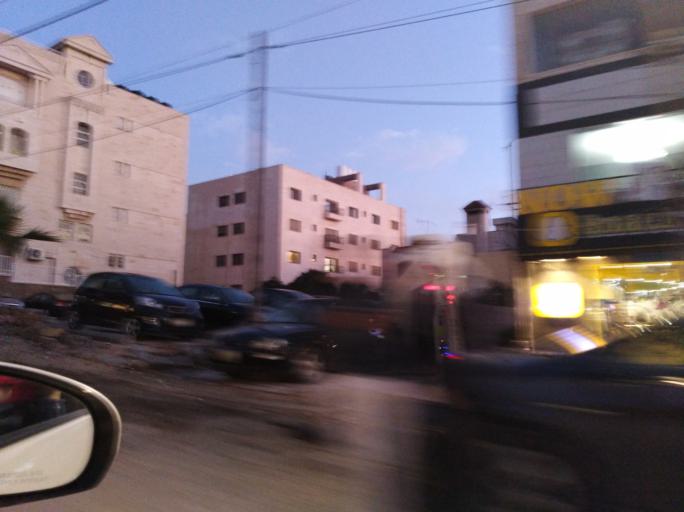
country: JO
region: Amman
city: Wadi as Sir
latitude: 31.9553
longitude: 35.8609
